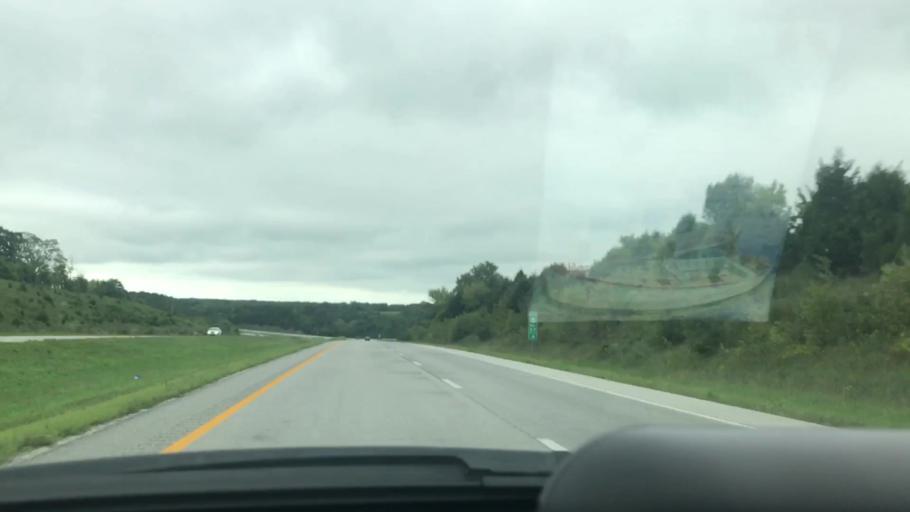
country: US
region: Missouri
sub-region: Greene County
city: Strafford
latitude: 37.2870
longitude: -93.1894
